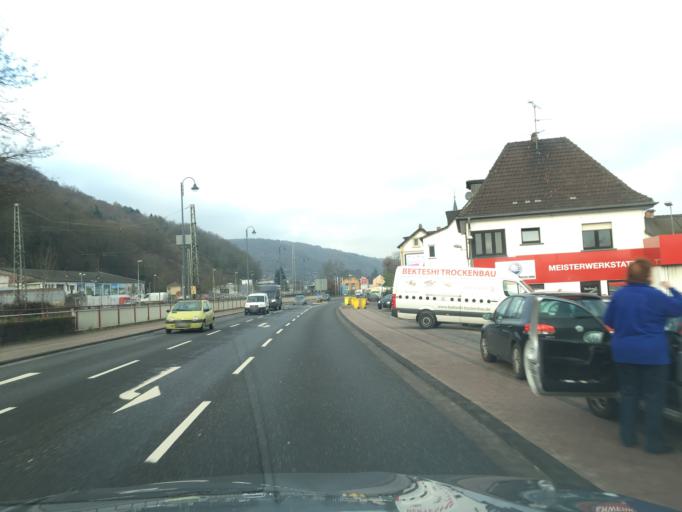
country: DE
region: Rheinland-Pfalz
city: Bad Honningen
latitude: 50.5023
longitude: 7.3080
